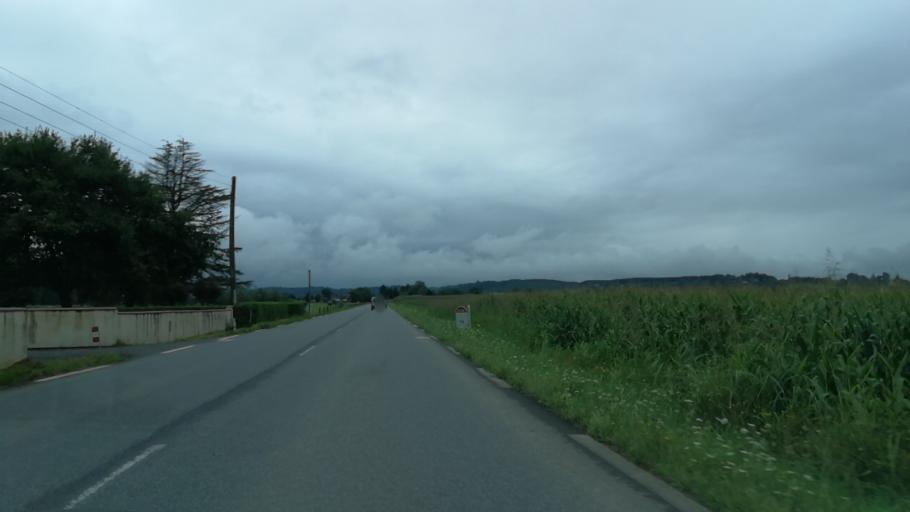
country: FR
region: Aquitaine
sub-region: Departement des Pyrenees-Atlantiques
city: Oloron-Sainte-Marie
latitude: 43.1354
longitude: -0.6066
